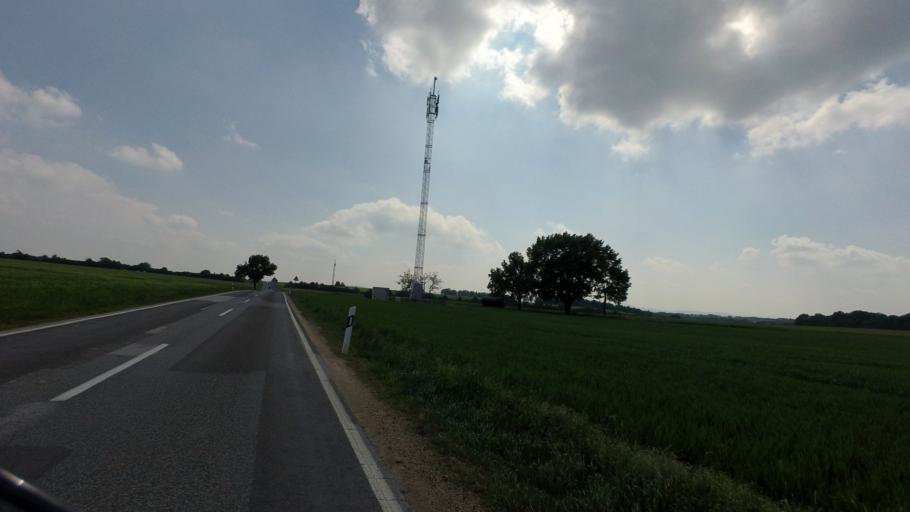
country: DE
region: Saxony
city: Weissenberg
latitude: 51.2150
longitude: 14.6640
